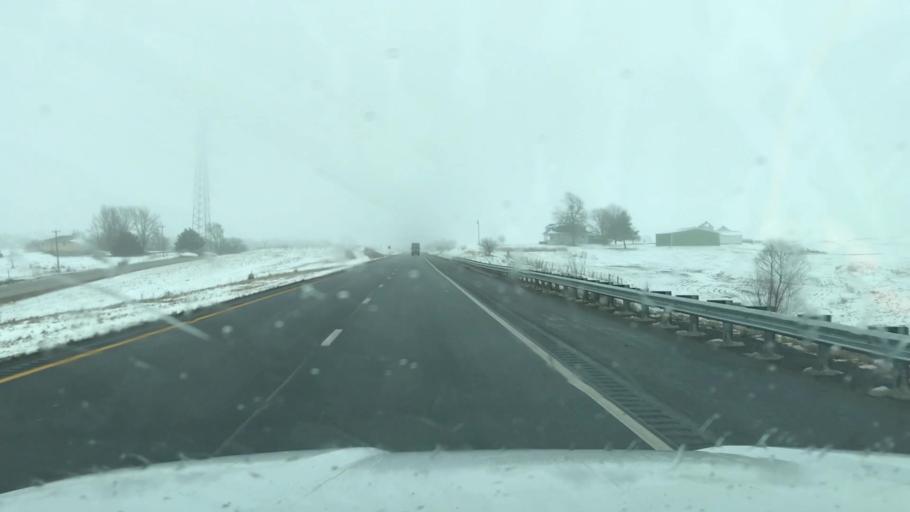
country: US
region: Missouri
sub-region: Clinton County
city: Gower
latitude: 39.7616
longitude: -94.5406
